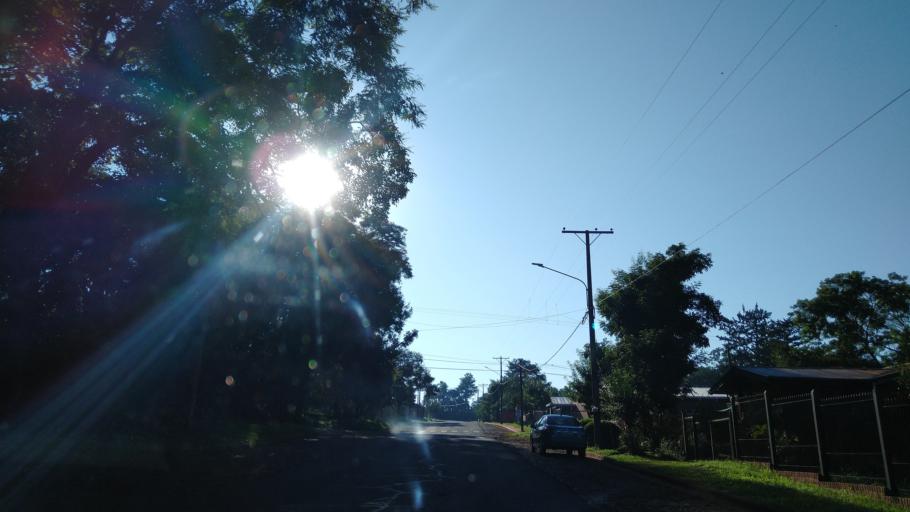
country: AR
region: Misiones
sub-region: Departamento de Montecarlo
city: Montecarlo
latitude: -26.5718
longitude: -54.7536
